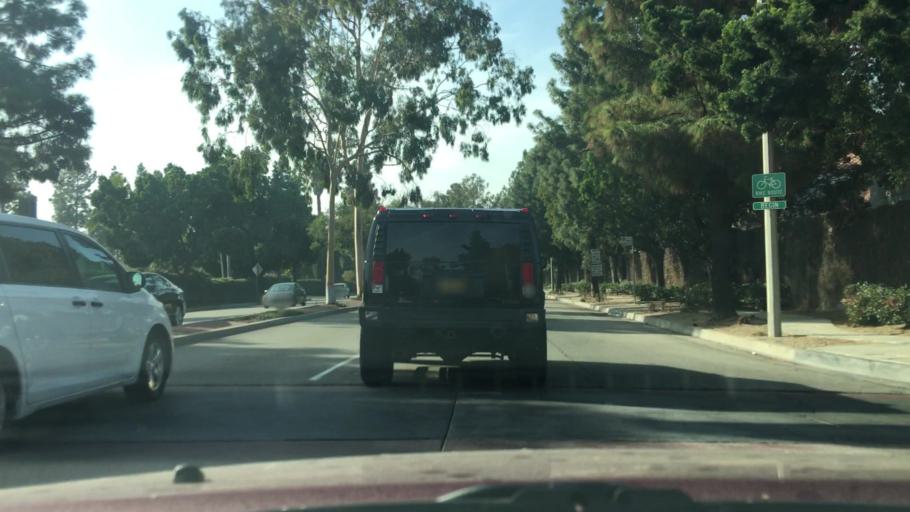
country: US
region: California
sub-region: Los Angeles County
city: Cerritos
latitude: 33.8733
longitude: -118.0553
